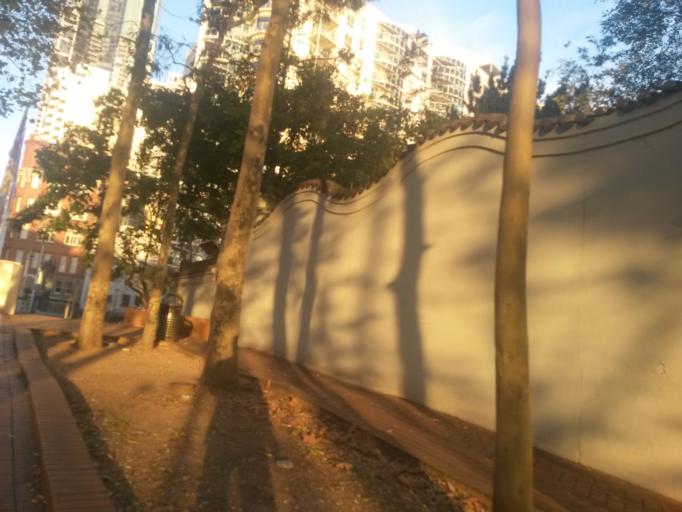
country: AU
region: New South Wales
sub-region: City of Sydney
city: Haymarket
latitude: -33.8760
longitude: 151.2030
